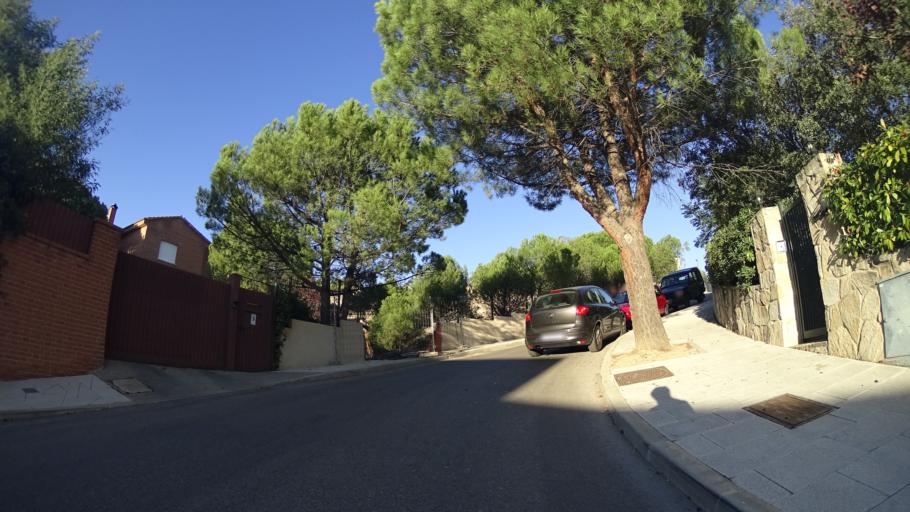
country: ES
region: Madrid
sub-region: Provincia de Madrid
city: Torrelodones
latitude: 40.5720
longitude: -3.9366
